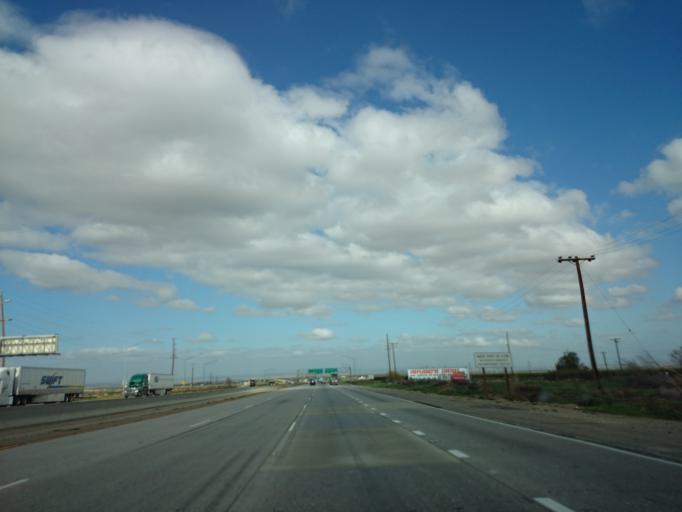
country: US
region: California
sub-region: Kern County
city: Frazier Park
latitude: 35.0039
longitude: -118.9507
